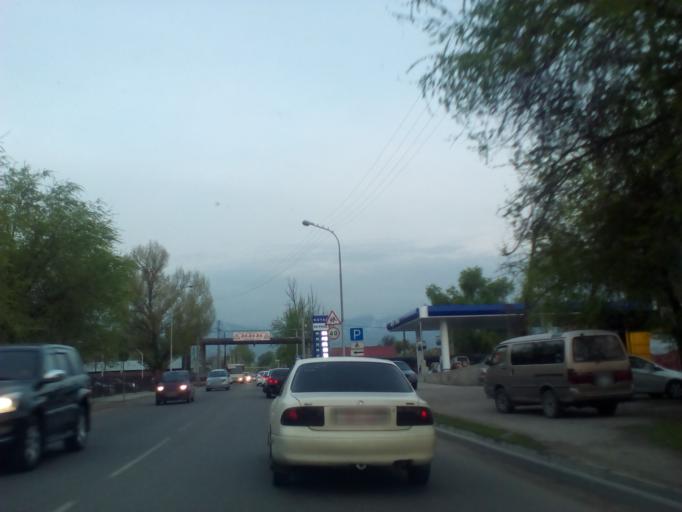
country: KZ
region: Almaty Qalasy
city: Almaty
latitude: 43.2343
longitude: 76.8252
